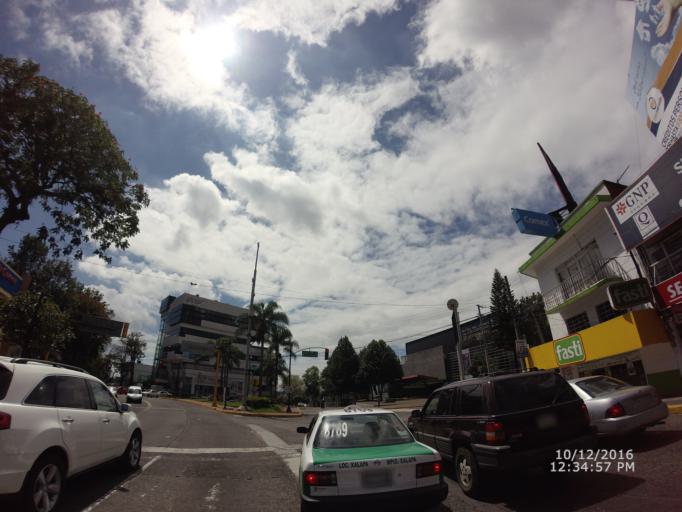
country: MX
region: Veracruz
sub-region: Xalapa
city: Xalapa de Enriquez
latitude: 19.5339
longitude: -96.9334
